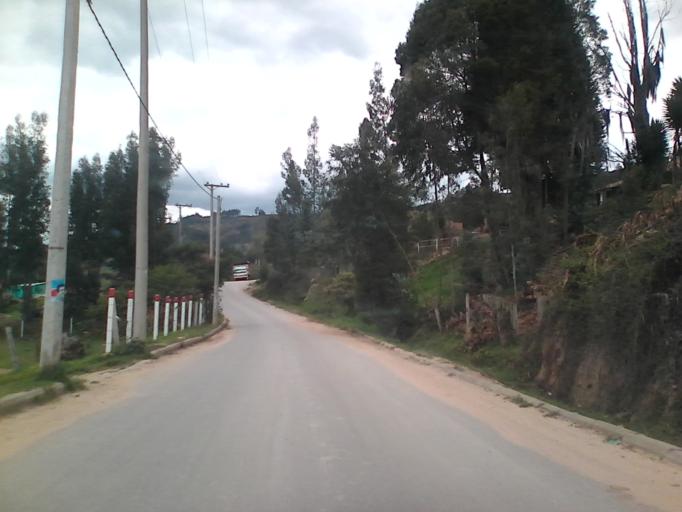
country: CO
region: Boyaca
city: Duitama
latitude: 5.8274
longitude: -73.0753
